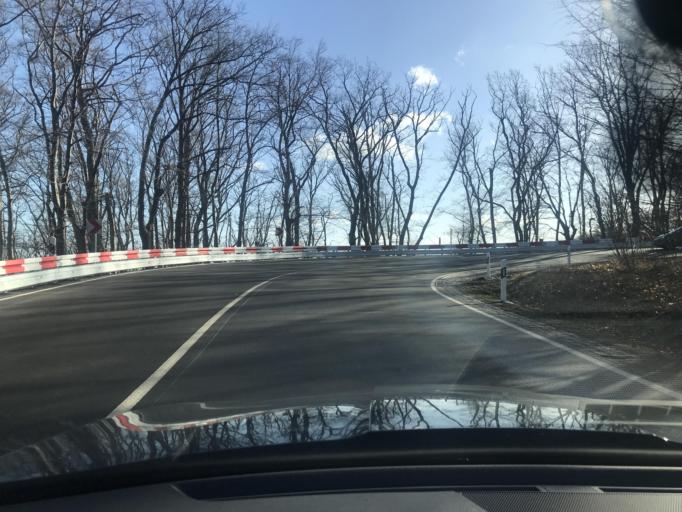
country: DE
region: Saxony-Anhalt
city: Blankenburg
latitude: 51.7877
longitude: 10.9431
